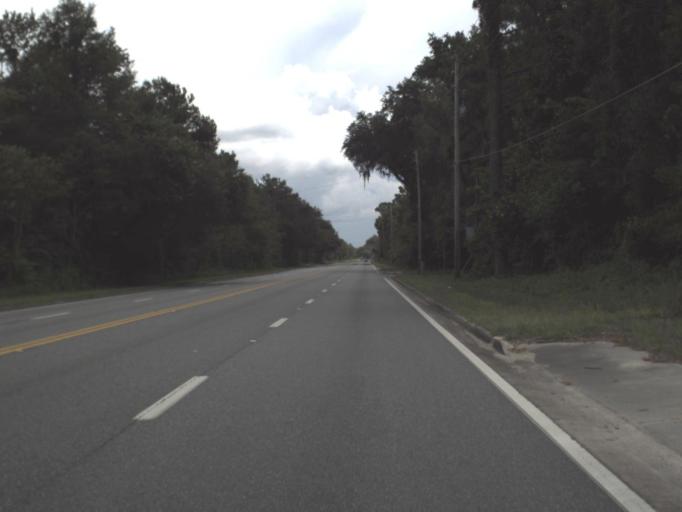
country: US
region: Florida
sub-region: Taylor County
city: Perry
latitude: 30.0939
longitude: -83.5427
